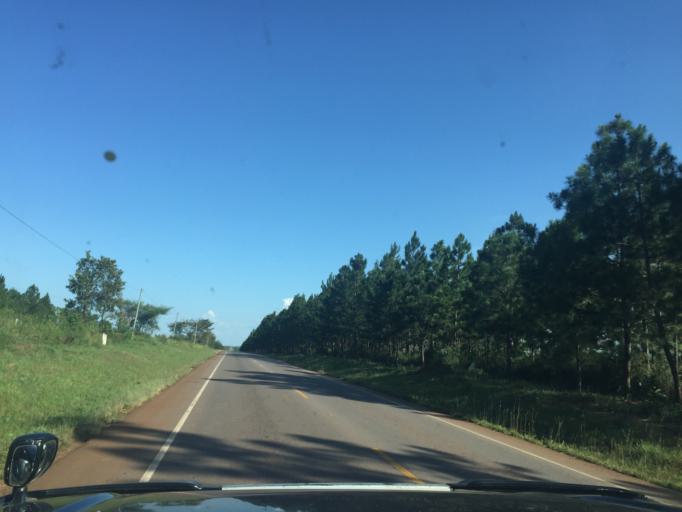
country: UG
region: Central Region
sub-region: Nakasongola District
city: Nakasongola
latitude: 1.3770
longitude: 32.3440
